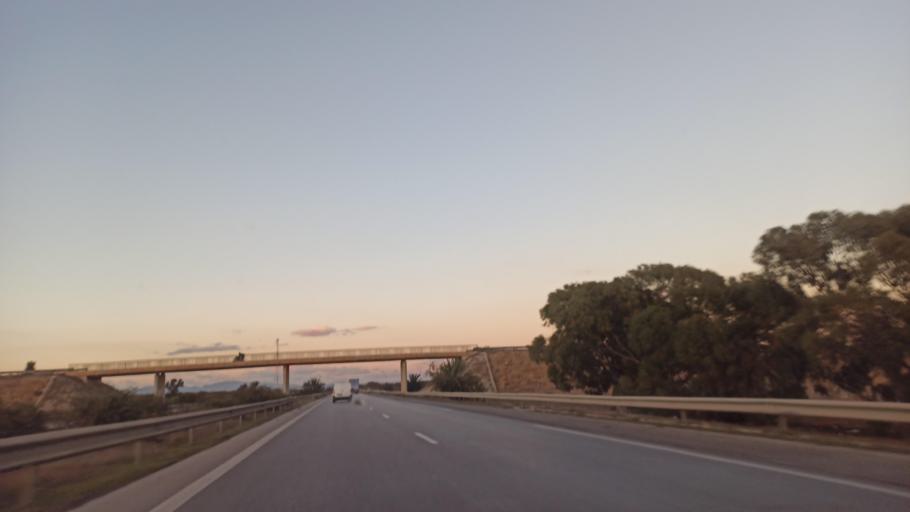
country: TN
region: Nabul
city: Al Hammamat
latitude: 36.2622
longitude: 10.4292
